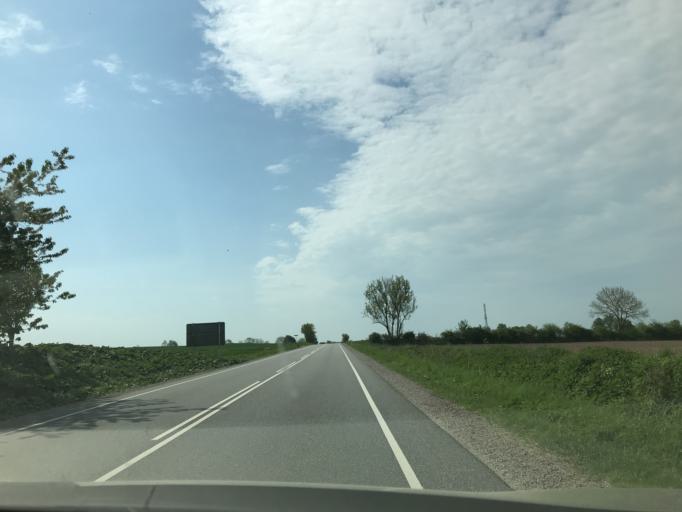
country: DK
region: South Denmark
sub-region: Middelfart Kommune
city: Ejby
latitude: 55.3826
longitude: 9.9178
